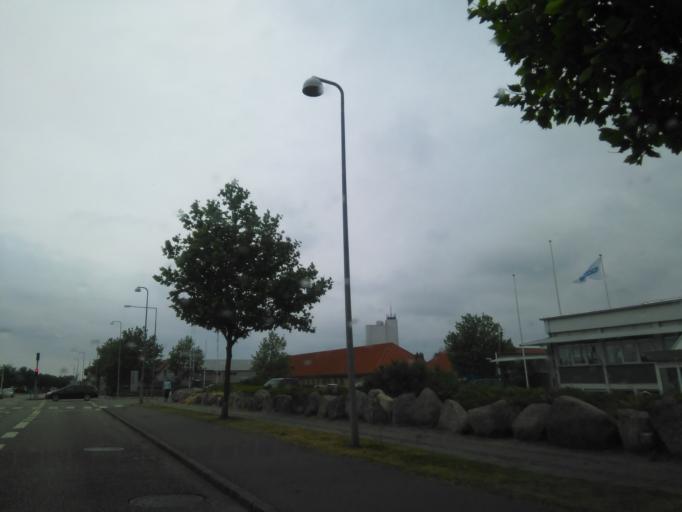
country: DK
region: Capital Region
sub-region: Bornholm Kommune
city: Ronne
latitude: 55.0957
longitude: 14.7190
